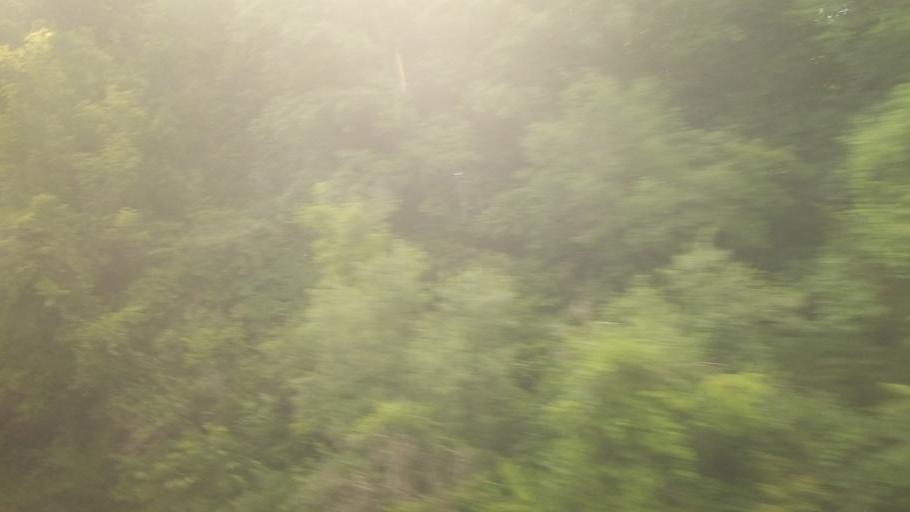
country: US
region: Kansas
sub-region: Johnson County
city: De Soto
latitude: 38.9854
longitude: -94.9136
